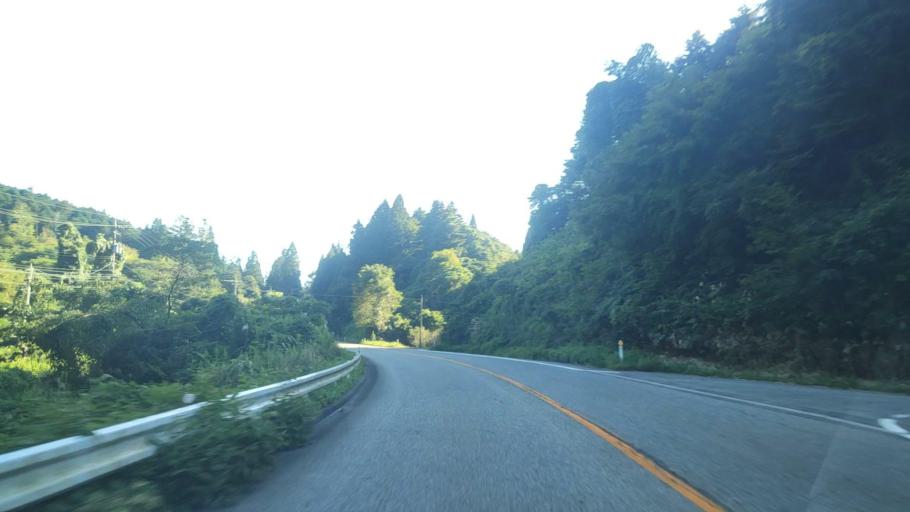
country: JP
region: Ishikawa
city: Nanao
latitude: 37.1380
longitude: 136.8631
